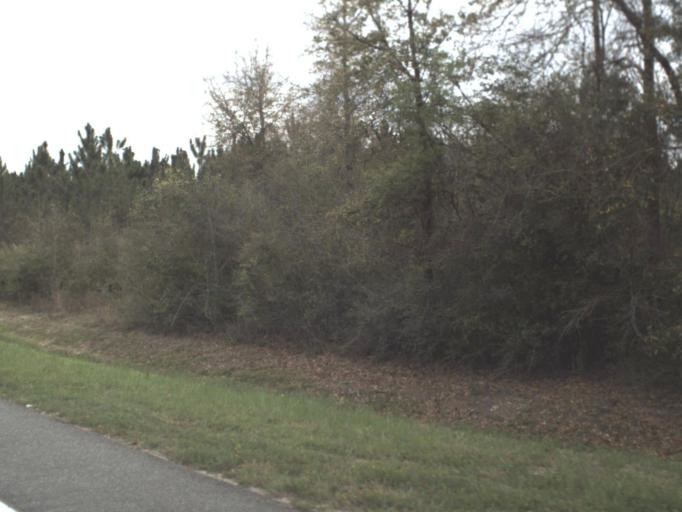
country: US
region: Florida
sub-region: Gulf County
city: Wewahitchka
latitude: 30.2592
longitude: -85.2360
